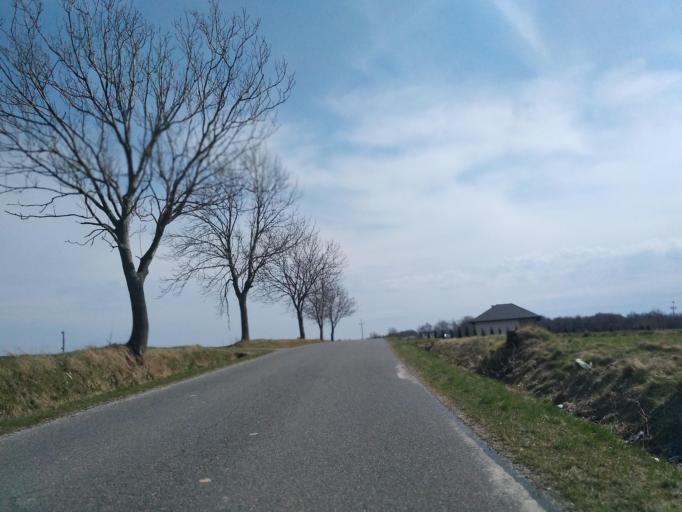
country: PL
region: Subcarpathian Voivodeship
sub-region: Powiat ropczycko-sedziszowski
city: Iwierzyce
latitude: 49.9844
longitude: 21.7363
